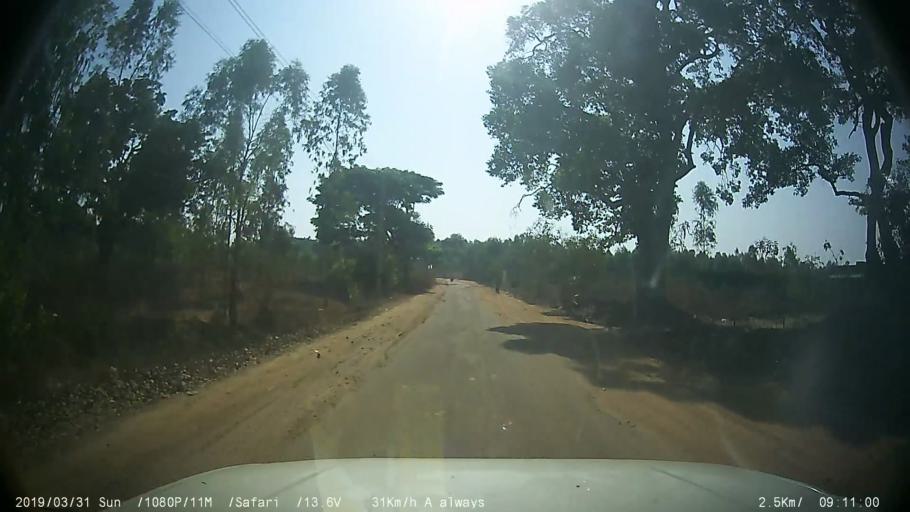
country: IN
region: Karnataka
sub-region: Bangalore Urban
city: Anekal
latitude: 12.8139
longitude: 77.6350
